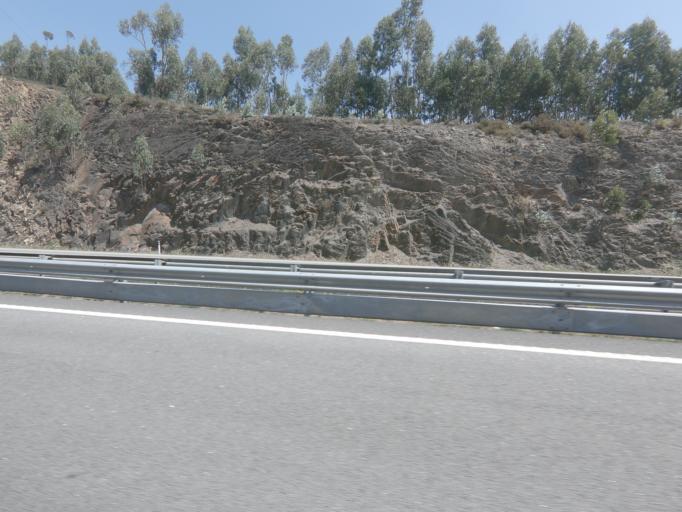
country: PT
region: Porto
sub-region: Valongo
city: Valongo
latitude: 41.2008
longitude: -8.5200
